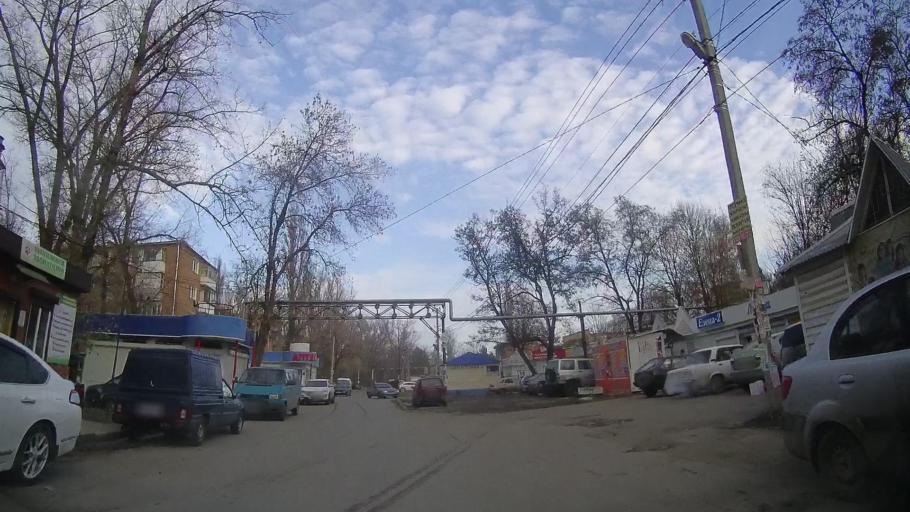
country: RU
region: Rostov
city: Bataysk
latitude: 47.1267
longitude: 39.7788
